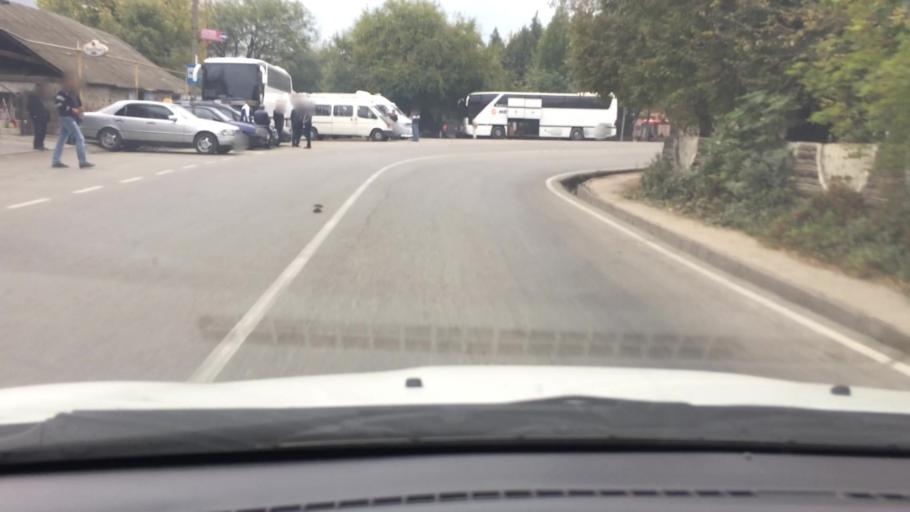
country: AM
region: Tavush
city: Bagratashen
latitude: 41.2466
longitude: 44.7992
